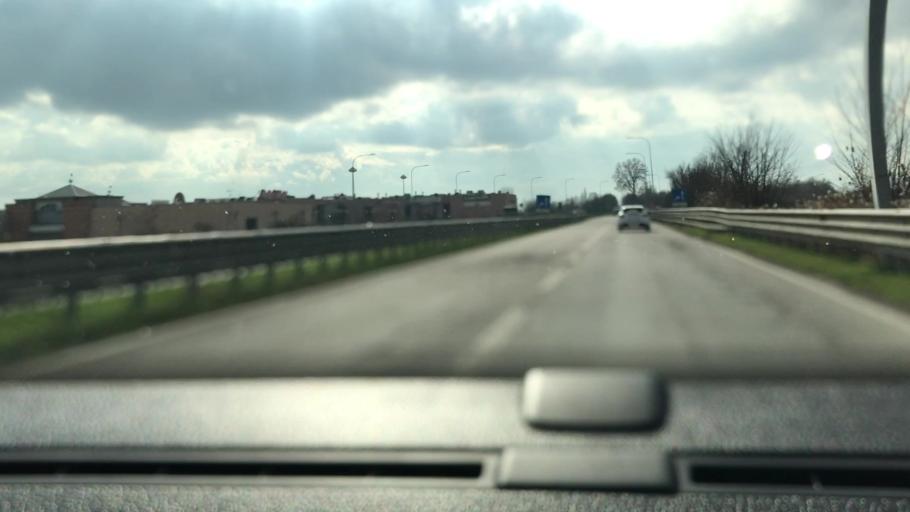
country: IT
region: Veneto
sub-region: Provincia di Rovigo
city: Grignano Polesine
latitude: 45.0318
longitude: 11.7776
